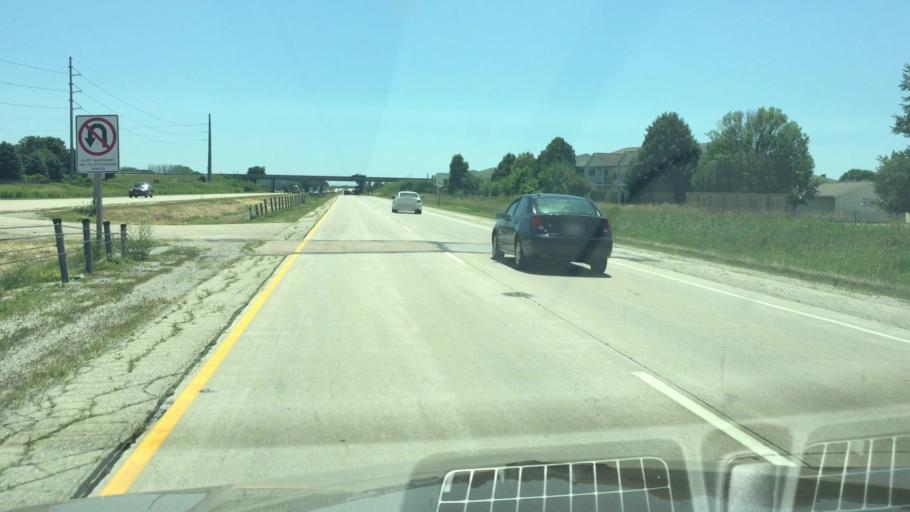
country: US
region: Wisconsin
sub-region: Dodge County
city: Beaver Dam
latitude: 43.4803
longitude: -88.8155
